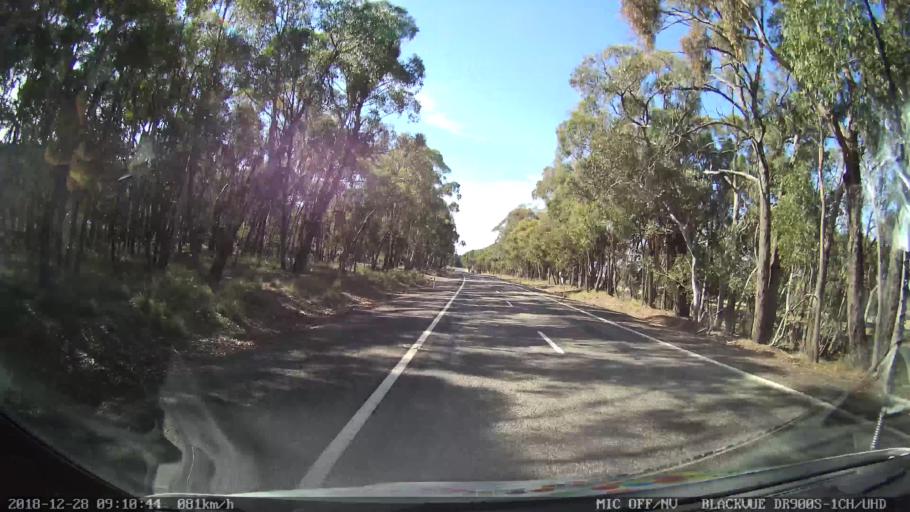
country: AU
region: New South Wales
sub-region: Upper Lachlan Shire
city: Crookwell
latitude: -34.2353
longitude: 149.3371
